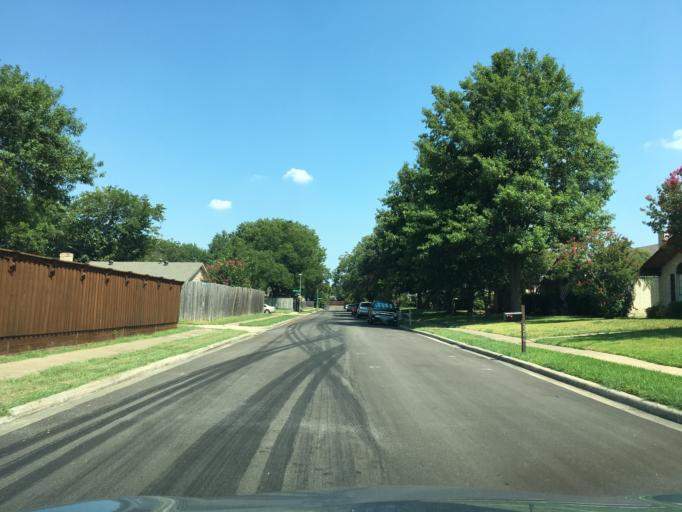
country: US
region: Texas
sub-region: Dallas County
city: Garland
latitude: 32.9335
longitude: -96.6628
